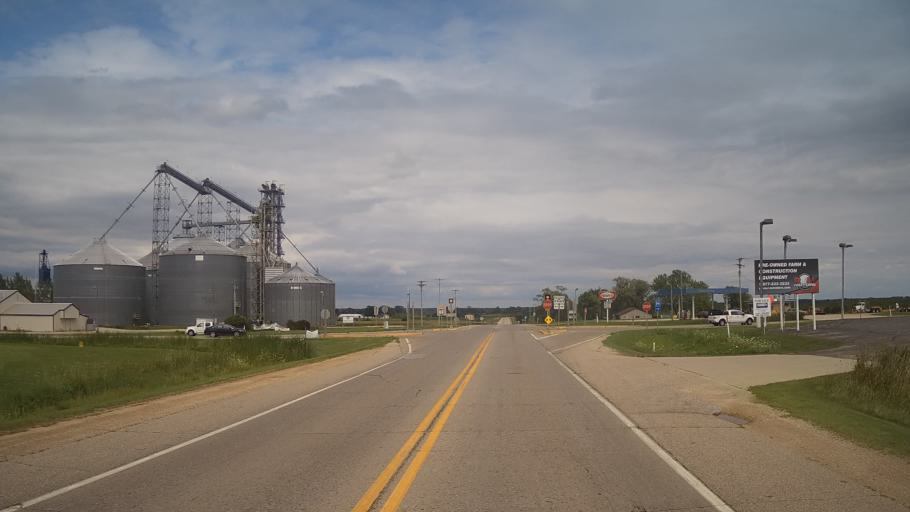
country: US
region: Wisconsin
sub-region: Green Lake County
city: Berlin
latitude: 44.0423
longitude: -88.9849
